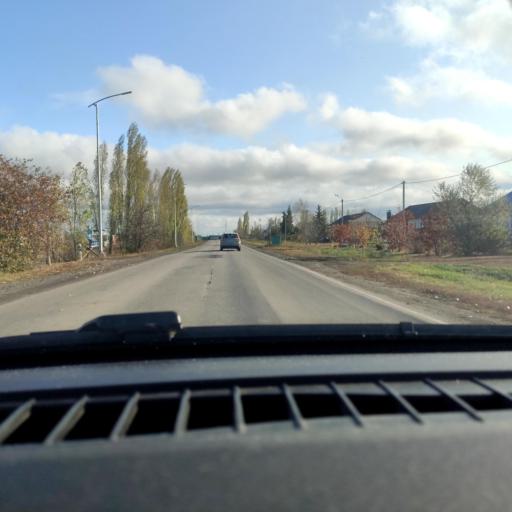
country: RU
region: Belgorod
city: Ilovka
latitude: 50.7304
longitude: 38.6856
